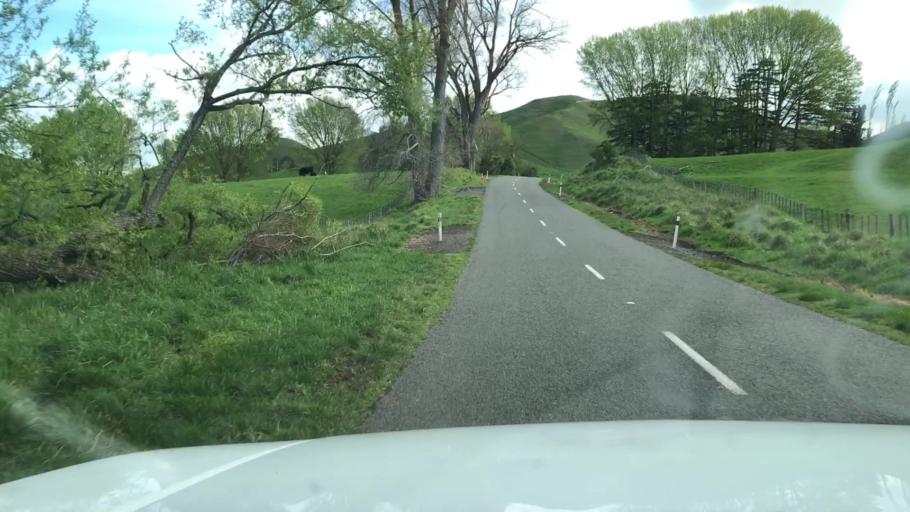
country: NZ
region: Hawke's Bay
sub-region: Hastings District
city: Hastings
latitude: -39.8201
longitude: 176.7389
